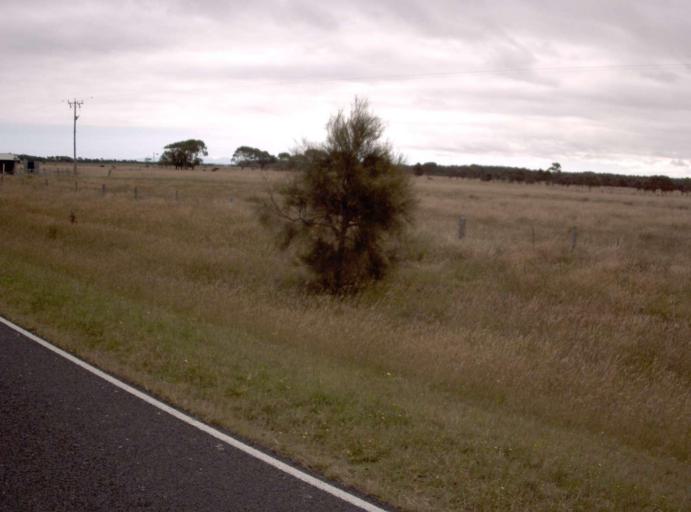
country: AU
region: Victoria
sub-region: Wellington
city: Sale
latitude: -38.5735
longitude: 146.8776
